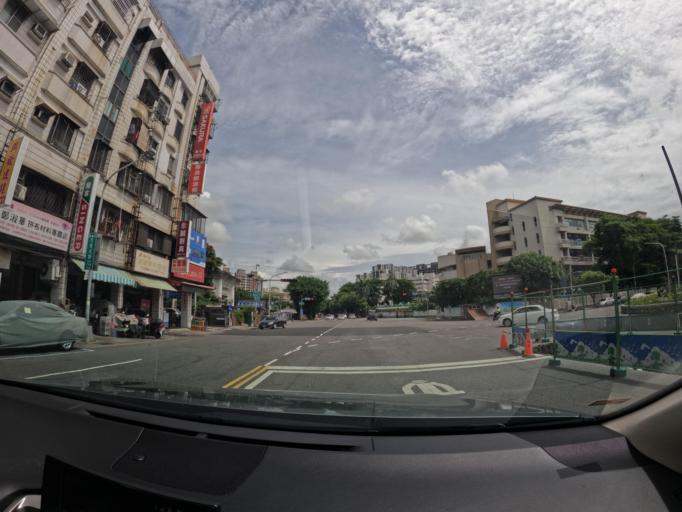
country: TW
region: Kaohsiung
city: Kaohsiung
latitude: 22.6757
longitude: 120.2867
